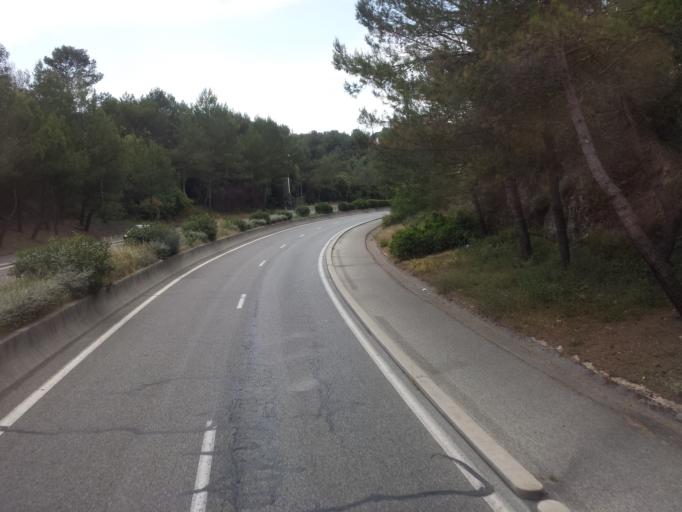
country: FR
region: Provence-Alpes-Cote d'Azur
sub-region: Departement des Alpes-Maritimes
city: Biot
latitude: 43.6106
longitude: 7.0816
